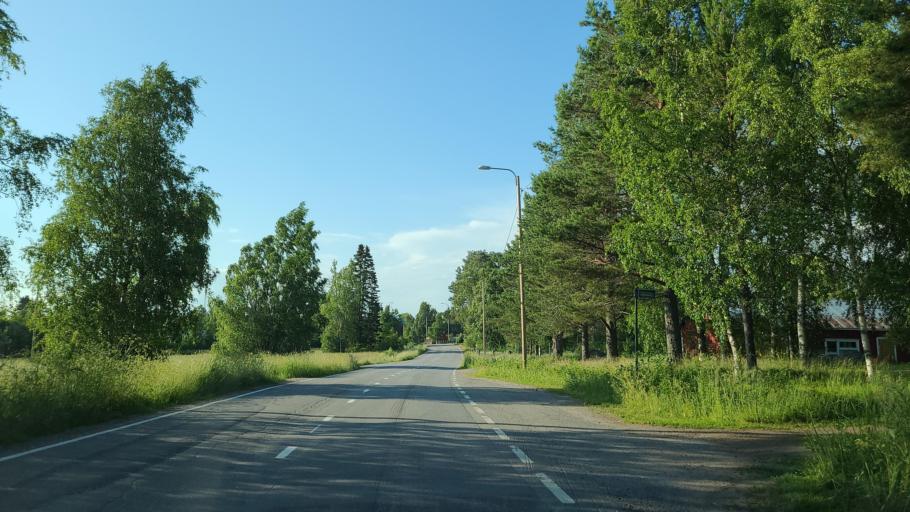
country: FI
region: Ostrobothnia
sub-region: Vaasa
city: Replot
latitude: 63.3375
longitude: 21.3319
